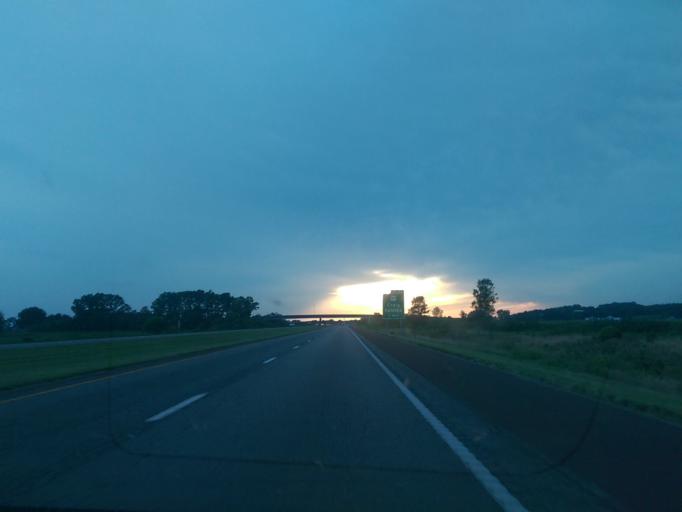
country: US
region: Missouri
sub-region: Holt County
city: Mound City
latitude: 40.1859
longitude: -95.3376
